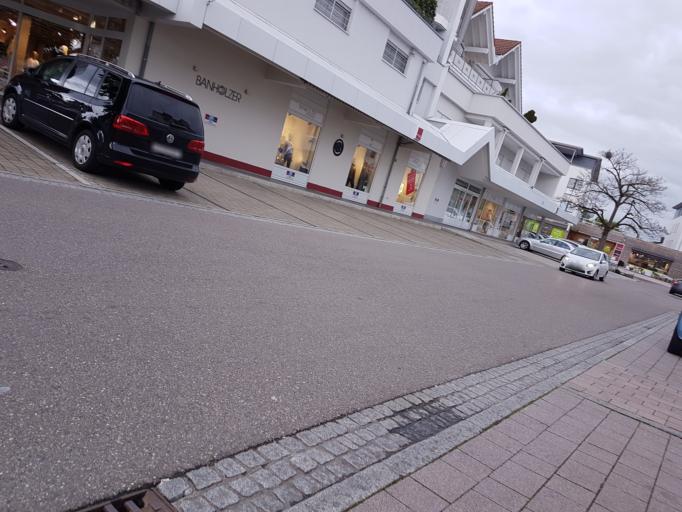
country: DE
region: Baden-Wuerttemberg
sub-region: Freiburg Region
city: Lauchringen
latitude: 47.6290
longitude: 8.3030
